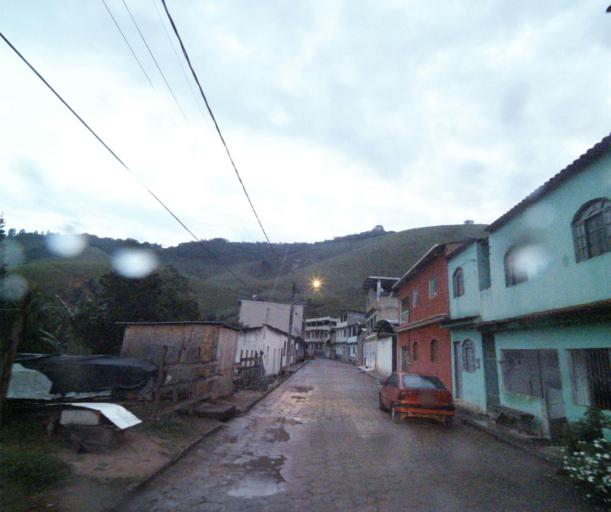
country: BR
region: Espirito Santo
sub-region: Muniz Freire
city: Muniz Freire
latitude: -20.4702
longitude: -41.4152
